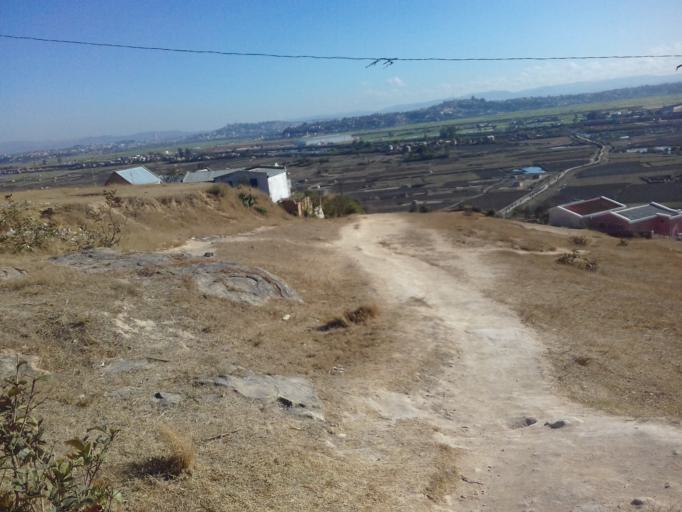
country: MG
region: Analamanga
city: Antananarivo
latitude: -18.8944
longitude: 47.4824
